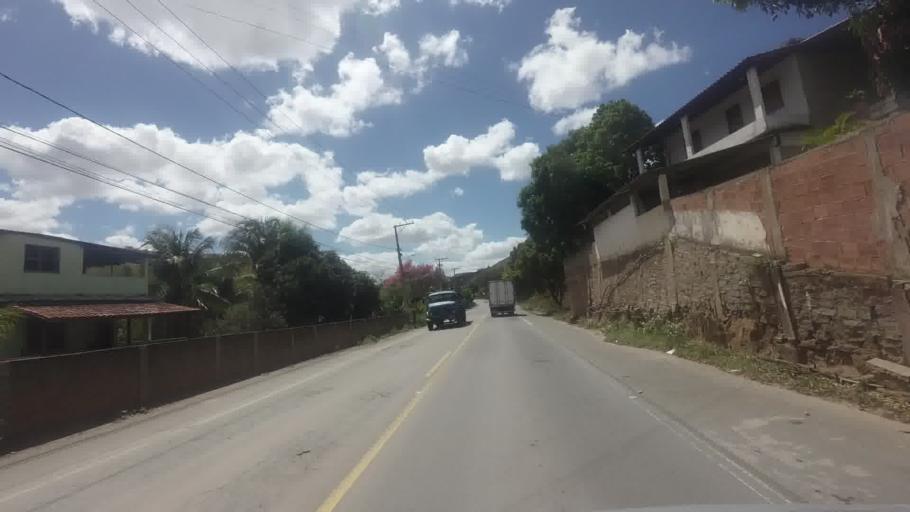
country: BR
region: Rio de Janeiro
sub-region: Santo Antonio De Padua
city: Santo Antonio de Padua
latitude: -21.6317
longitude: -42.2674
